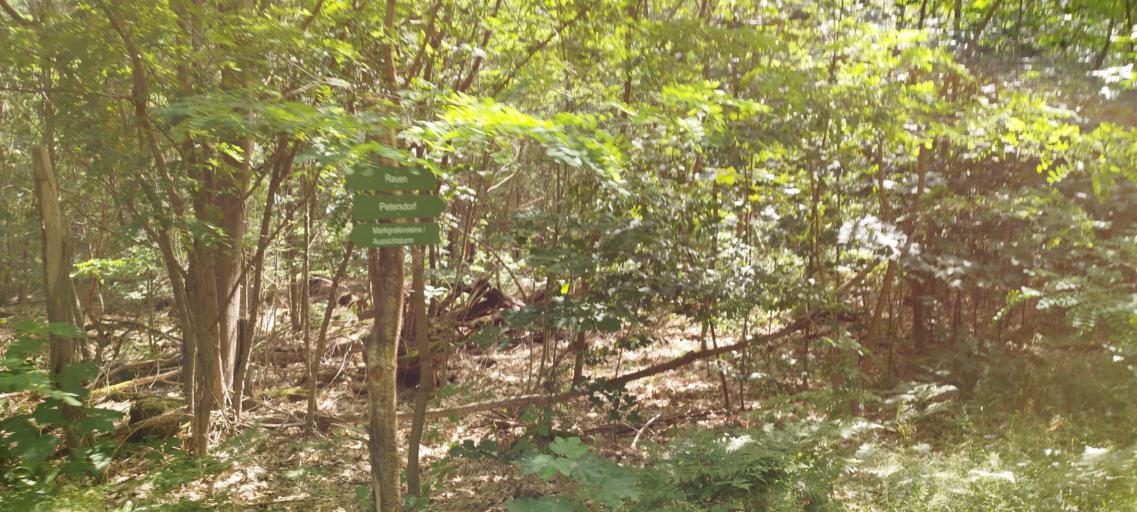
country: DE
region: Brandenburg
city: Bad Saarow
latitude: 52.3180
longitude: 14.0524
